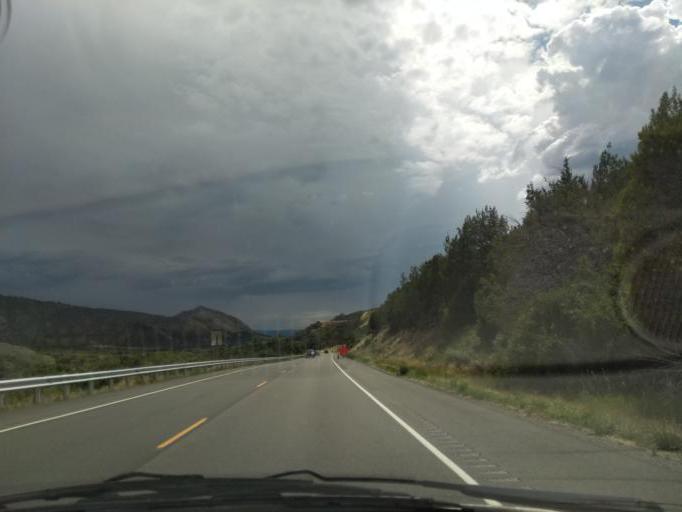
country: US
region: Colorado
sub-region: Delta County
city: Paonia
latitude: 38.9086
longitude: -107.5592
